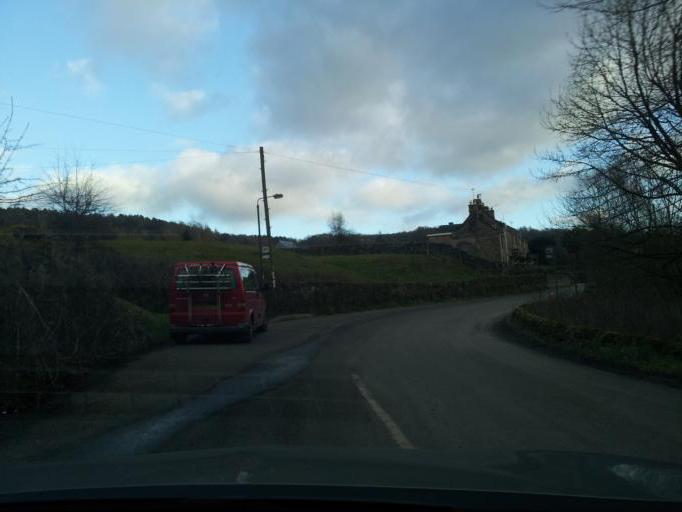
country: GB
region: England
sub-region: Derbyshire
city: Bakewell
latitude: 53.1608
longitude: -1.6554
